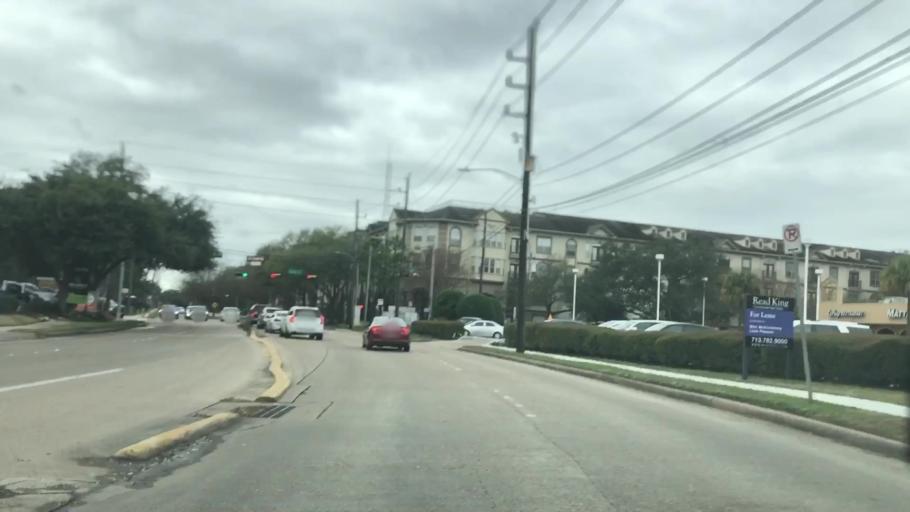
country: US
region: Texas
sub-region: Harris County
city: Hunters Creek Village
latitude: 29.7636
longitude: -95.4791
